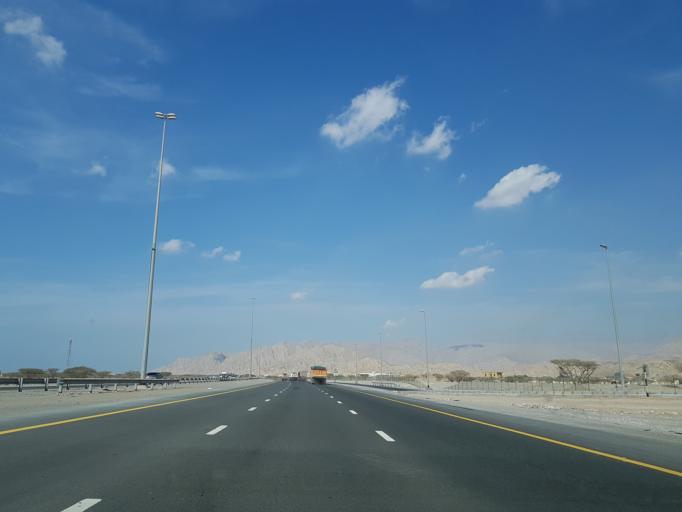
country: AE
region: Ra's al Khaymah
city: Ras al-Khaimah
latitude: 25.7807
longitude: 56.0312
